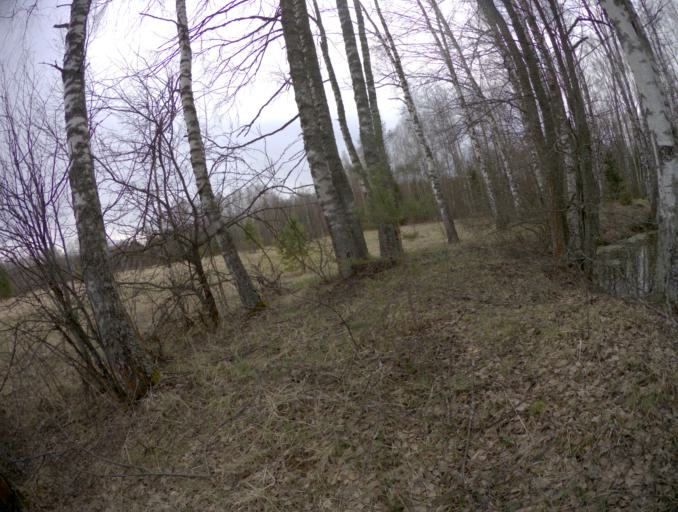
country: RU
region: Vladimir
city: Raduzhnyy
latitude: 55.8782
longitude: 40.2083
